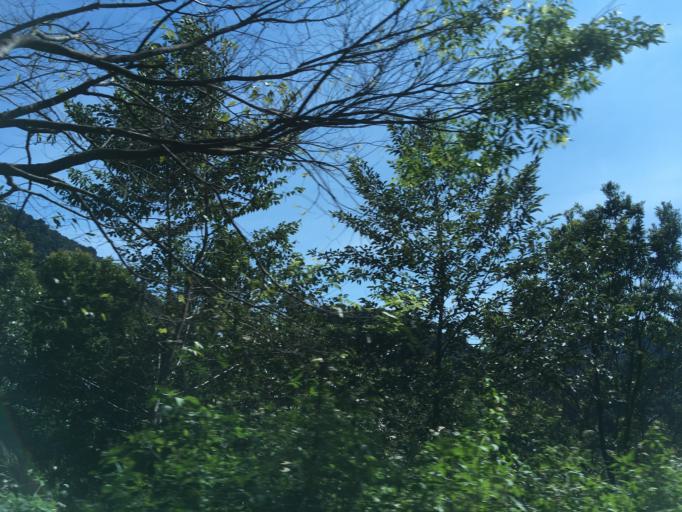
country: TW
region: Taiwan
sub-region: Yilan
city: Yilan
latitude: 24.4201
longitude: 121.7321
